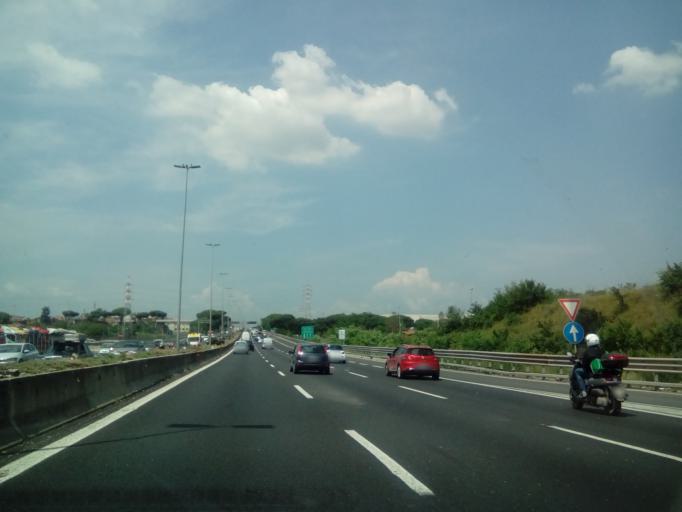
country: IT
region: Latium
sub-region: Citta metropolitana di Roma Capitale
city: Setteville
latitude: 41.9012
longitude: 12.6155
